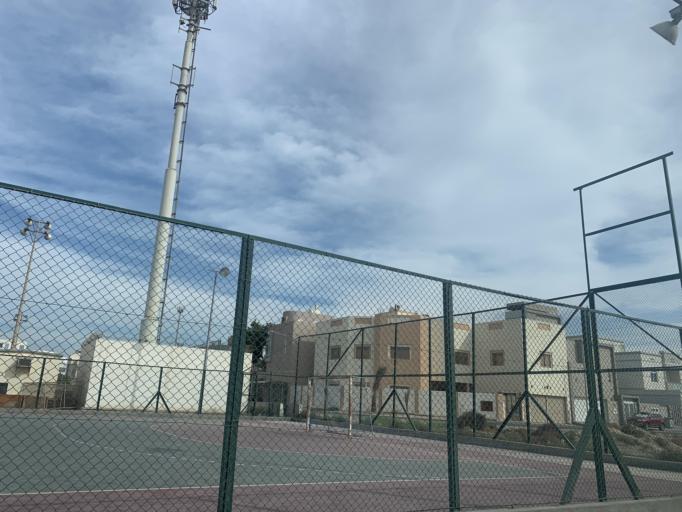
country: BH
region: Central Governorate
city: Madinat Hamad
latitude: 26.1179
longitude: 50.4761
